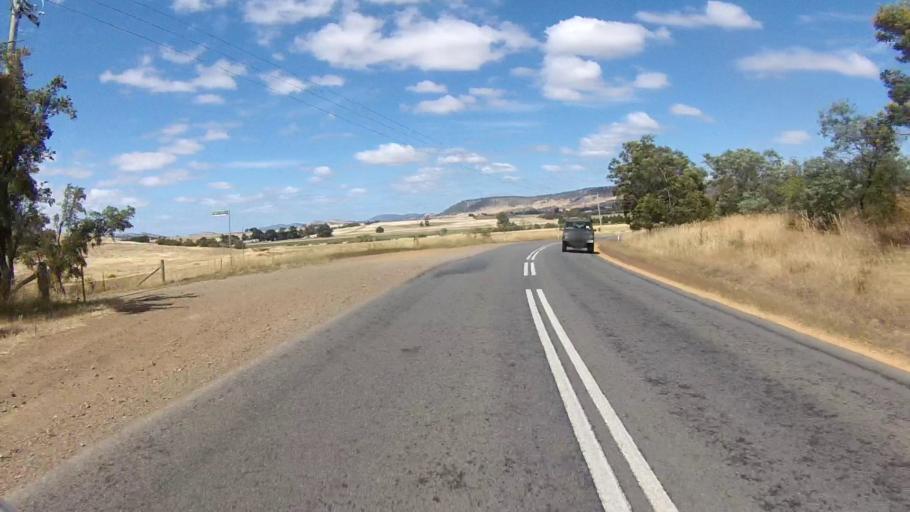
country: AU
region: Tasmania
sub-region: Clarence
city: Cambridge
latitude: -42.6535
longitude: 147.4334
